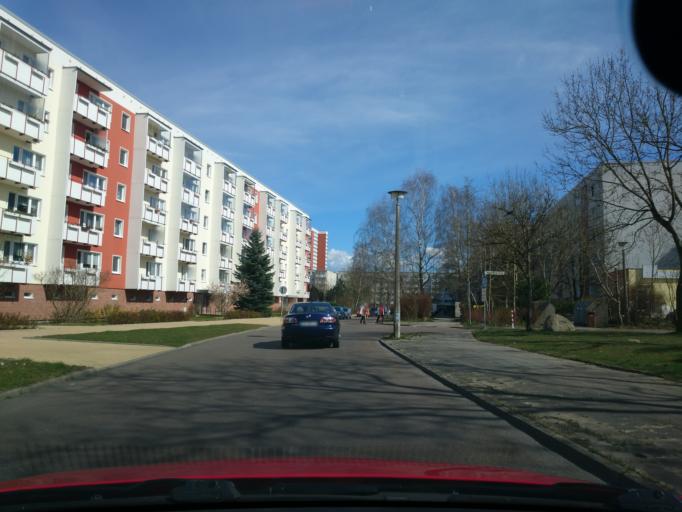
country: DE
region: Mecklenburg-Vorpommern
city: Lambrechtshagen
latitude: 54.1171
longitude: 12.0542
